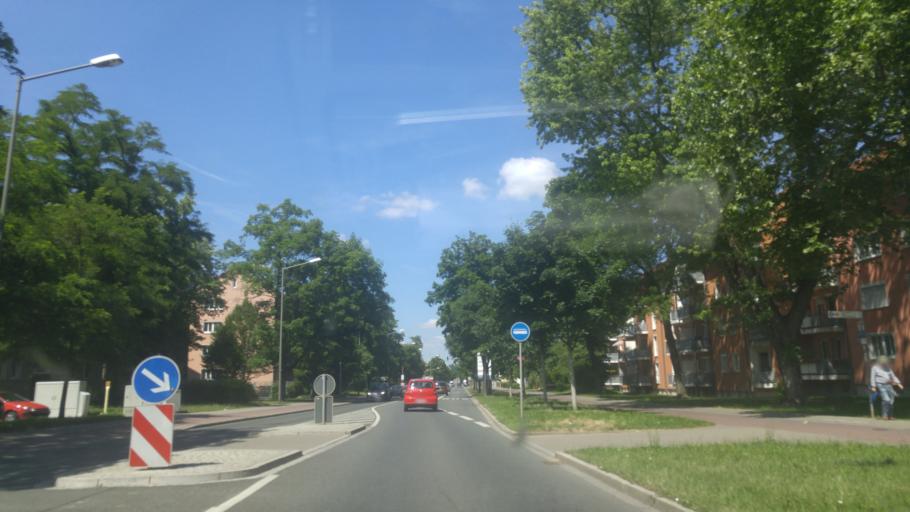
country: DE
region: Bavaria
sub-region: Regierungsbezirk Mittelfranken
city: Erlangen
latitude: 49.5834
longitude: 10.9937
